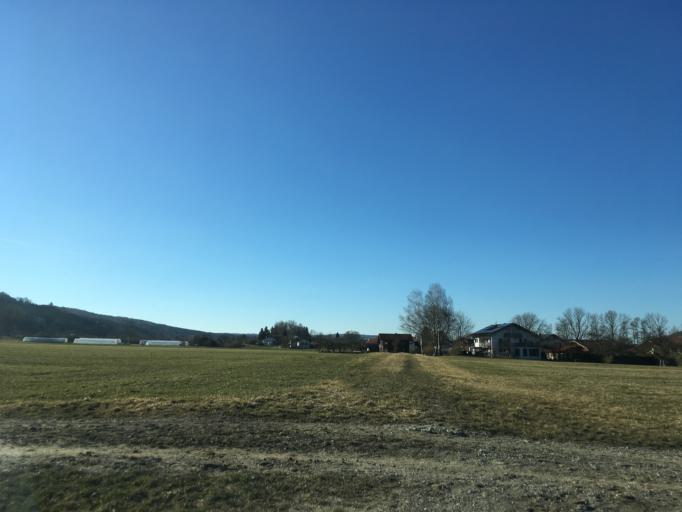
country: DE
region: Bavaria
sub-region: Upper Bavaria
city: Bruckmuhl
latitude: 47.8687
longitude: 11.9063
